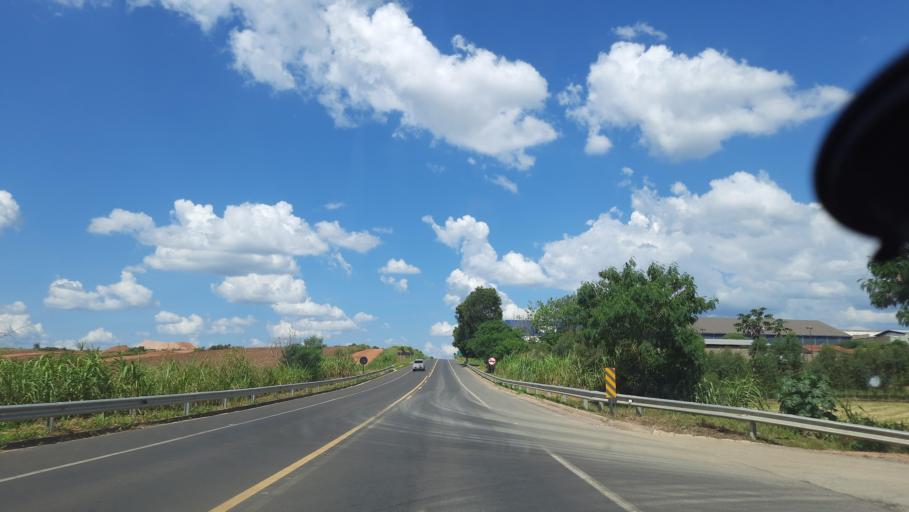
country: BR
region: Sao Paulo
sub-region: Sao Jose Do Rio Pardo
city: Sao Jose do Rio Pardo
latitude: -21.6033
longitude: -46.9237
